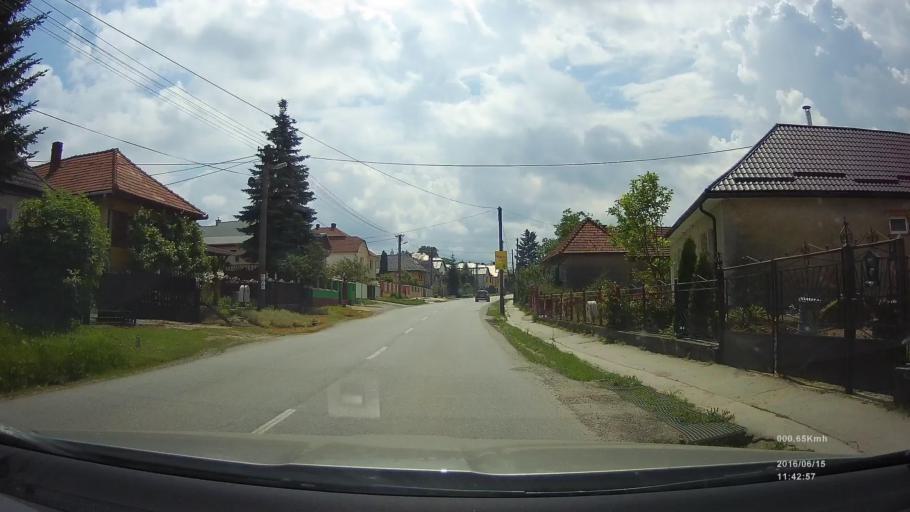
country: SK
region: Kosicky
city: Kosice
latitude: 48.7555
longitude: 21.3423
